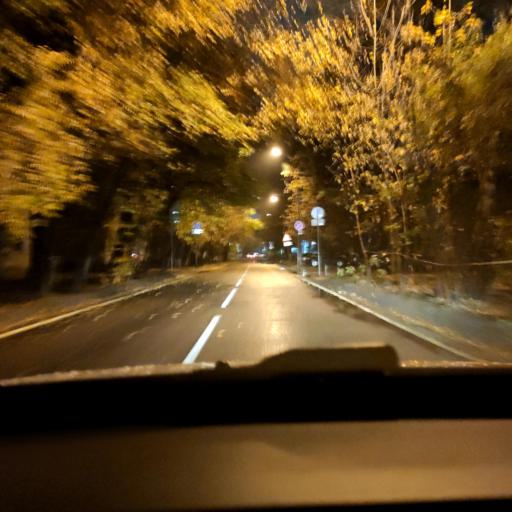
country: RU
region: Voronezj
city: Voronezh
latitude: 51.6612
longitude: 39.1818
